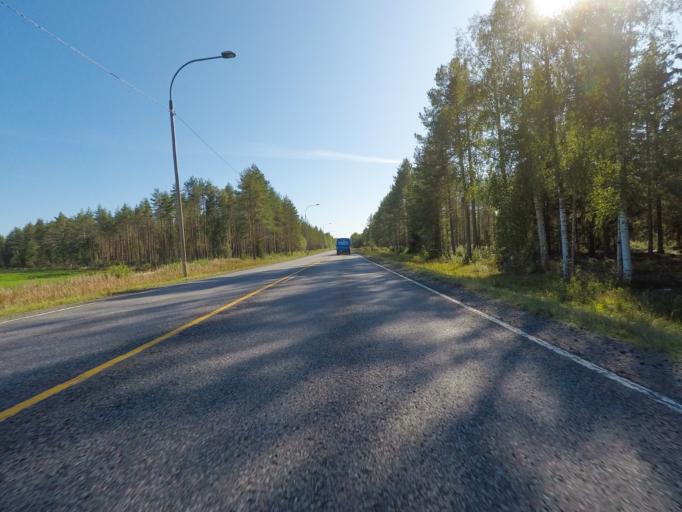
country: FI
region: Southern Savonia
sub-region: Pieksaemaeki
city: Joroinen
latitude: 62.1126
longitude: 27.8362
